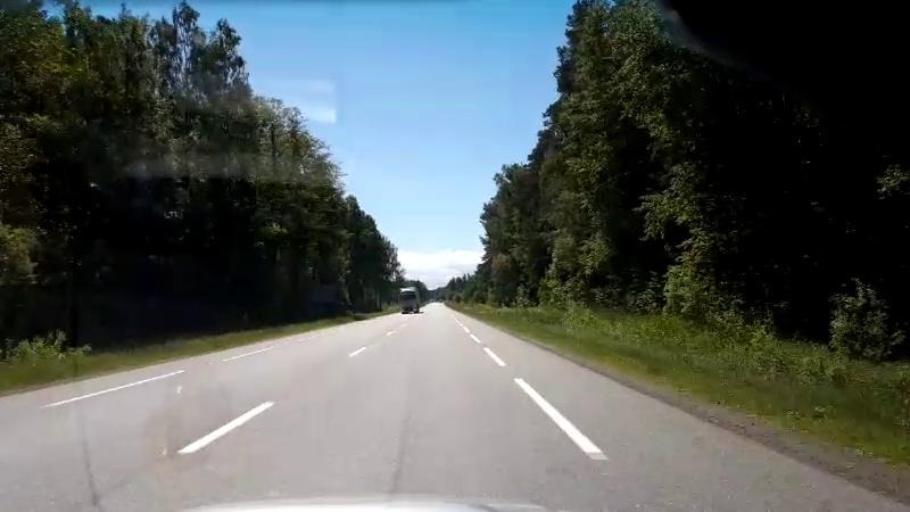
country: LV
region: Saulkrastu
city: Saulkrasti
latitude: 57.4276
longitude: 24.4293
